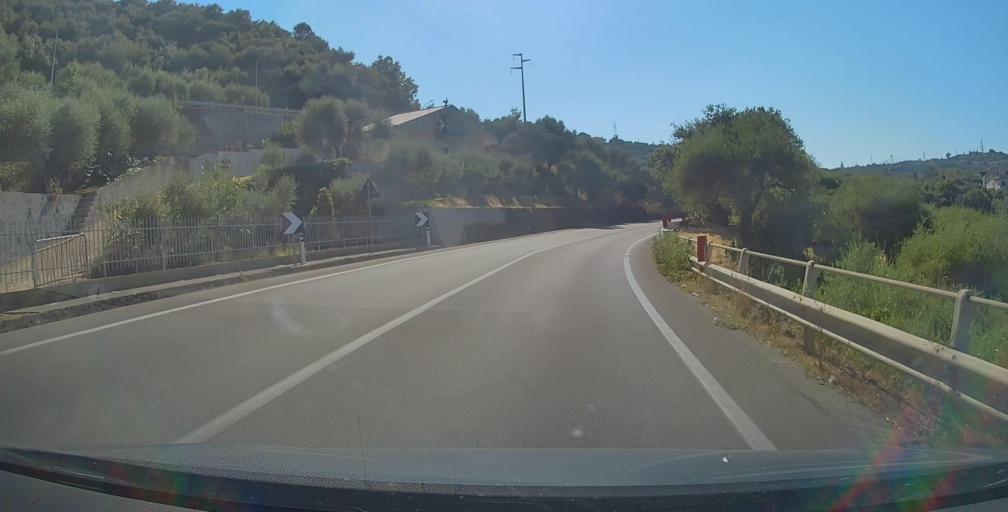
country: IT
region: Sicily
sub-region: Messina
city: Capo d'Orlando
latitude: 38.1518
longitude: 14.7658
